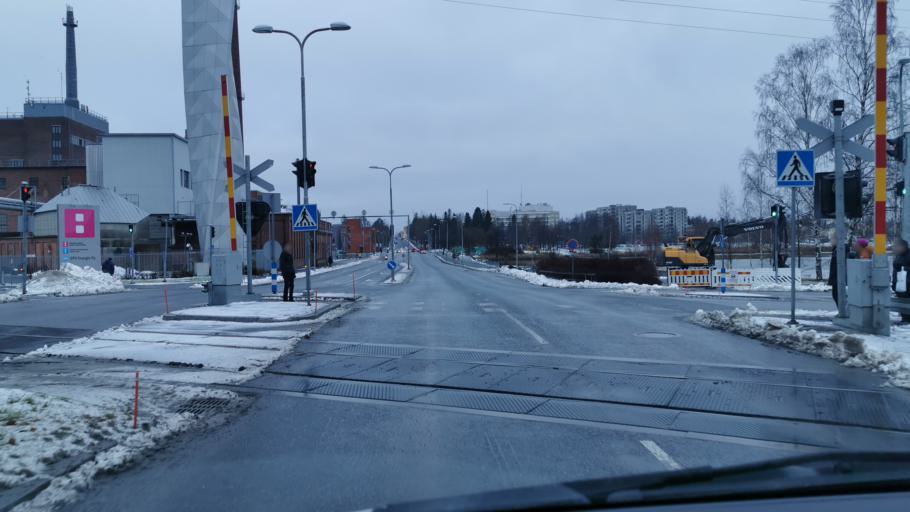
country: FI
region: Ostrobothnia
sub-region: Vaasa
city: Vaasa
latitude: 63.1010
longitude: 21.6045
